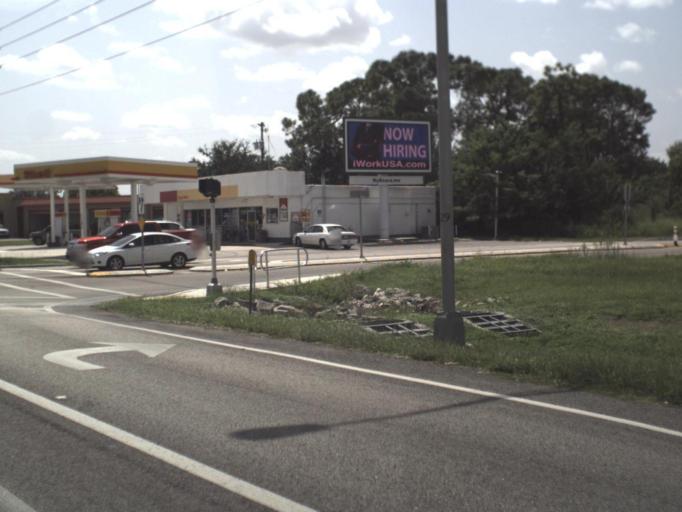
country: US
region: Florida
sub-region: Highlands County
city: Sebring
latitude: 27.4937
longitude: -81.4859
